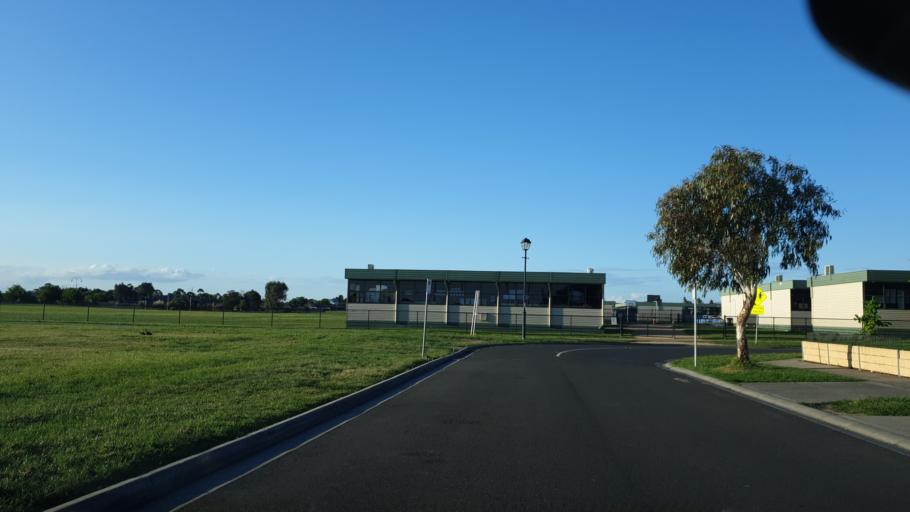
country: AU
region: Victoria
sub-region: Casey
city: Cranbourne East
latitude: -38.1066
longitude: 145.3035
